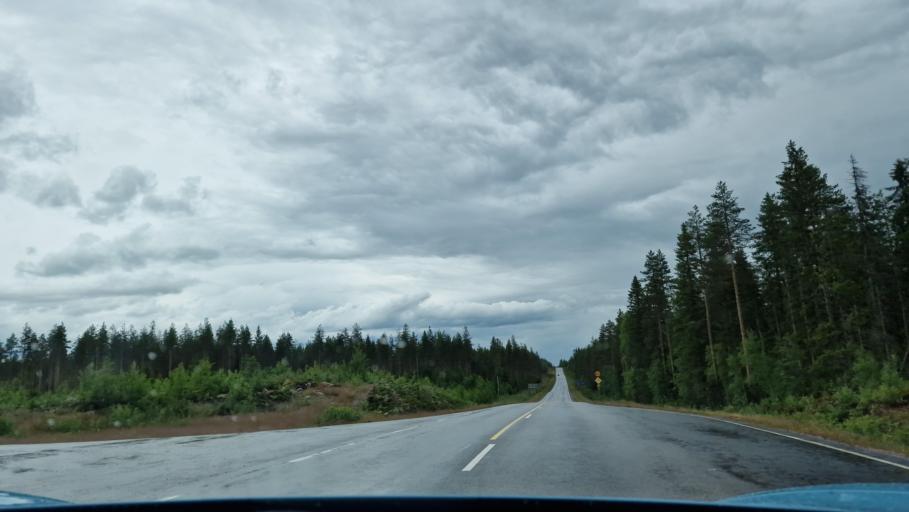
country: FI
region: Central Finland
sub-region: Saarijaervi-Viitasaari
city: Pylkoenmaeki
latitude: 62.6582
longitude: 24.5713
